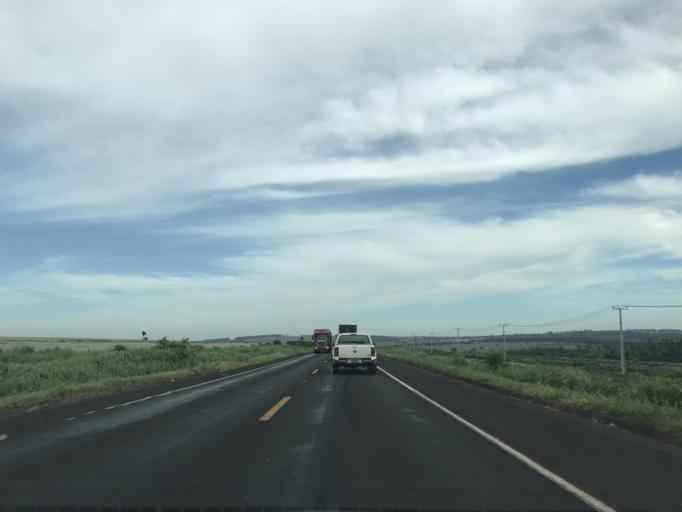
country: BR
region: Parana
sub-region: Paranavai
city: Paranavai
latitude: -23.0083
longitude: -52.5427
